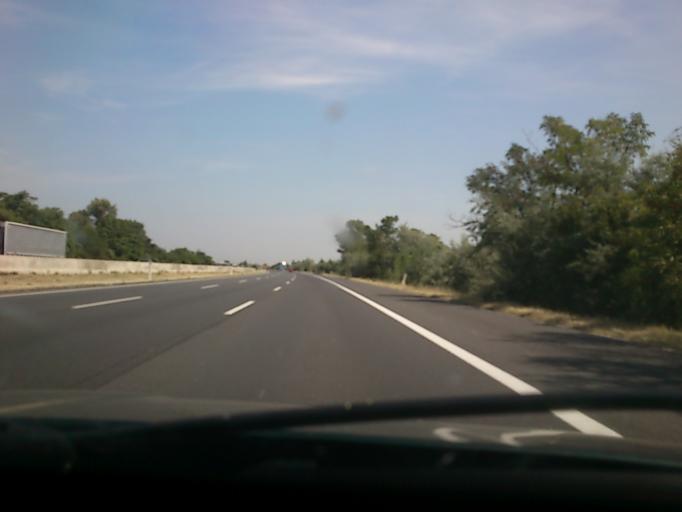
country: AT
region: Lower Austria
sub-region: Politischer Bezirk Wiener Neustadt
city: Felixdorf
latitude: 47.8784
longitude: 16.2024
